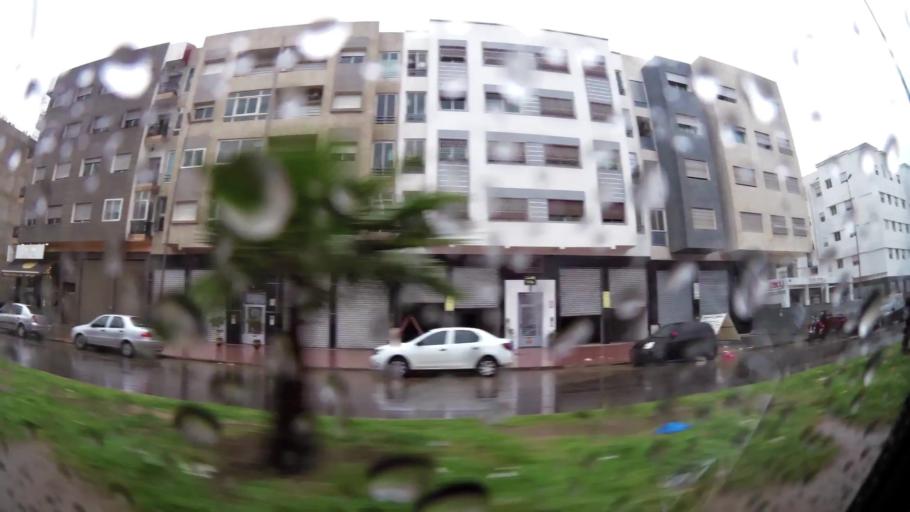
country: MA
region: Grand Casablanca
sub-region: Mediouna
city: Tit Mellil
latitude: 33.5951
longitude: -7.4988
